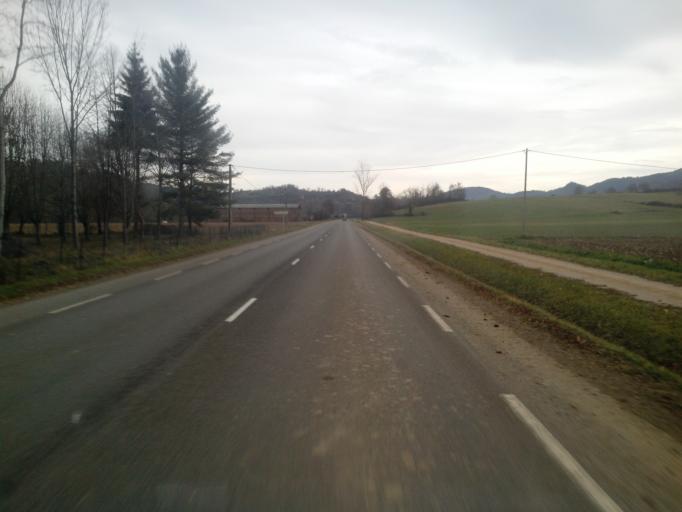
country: FR
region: Midi-Pyrenees
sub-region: Departement de l'Ariege
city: Foix
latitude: 43.0176
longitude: 1.3960
